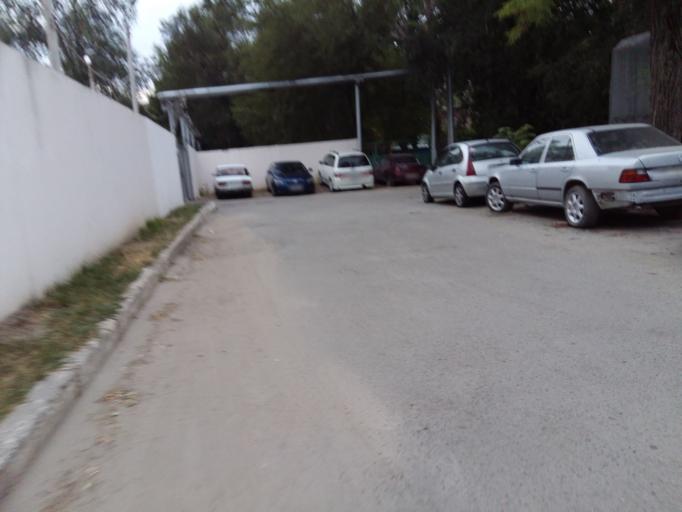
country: RU
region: Rostov
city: Imeni Chkalova
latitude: 47.2767
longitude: 39.7406
